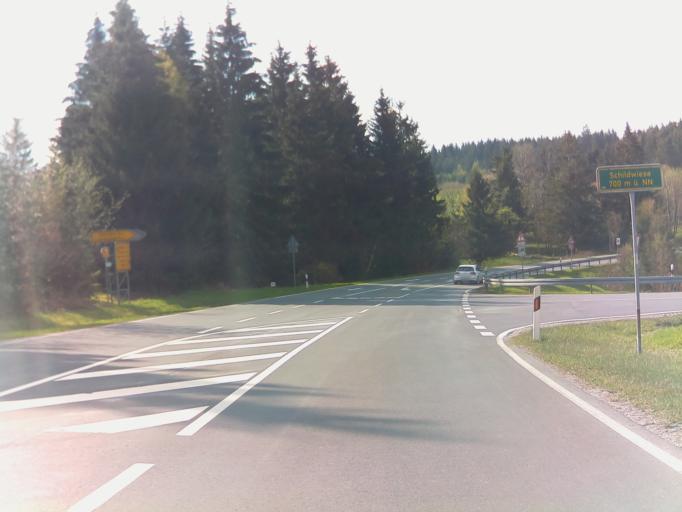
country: DE
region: Bavaria
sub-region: Upper Franconia
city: Tettau
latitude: 50.4820
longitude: 11.2991
